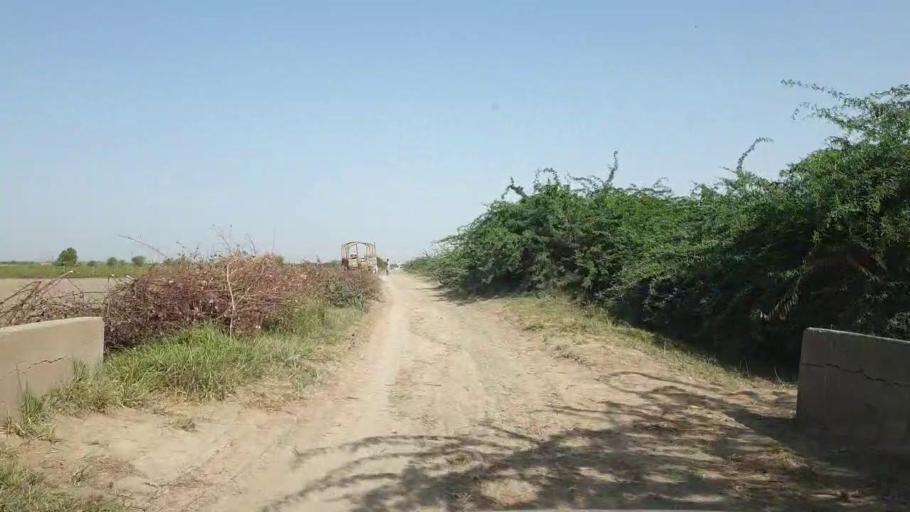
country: PK
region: Sindh
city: Tando Bago
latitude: 24.7035
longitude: 69.0709
